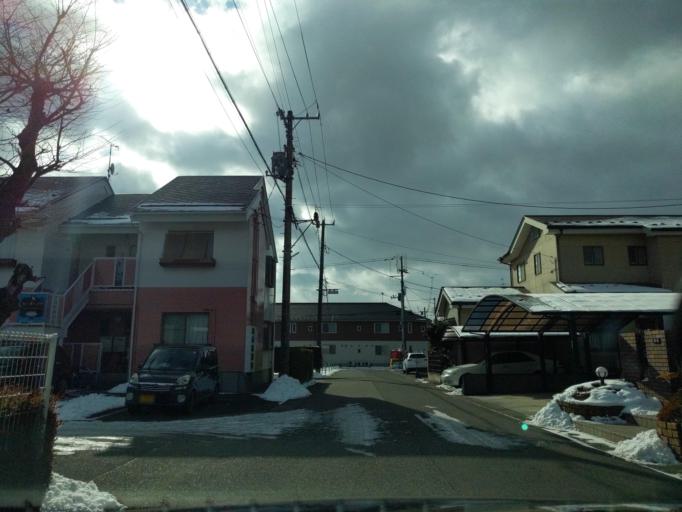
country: JP
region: Fukushima
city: Koriyama
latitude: 37.4199
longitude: 140.3501
